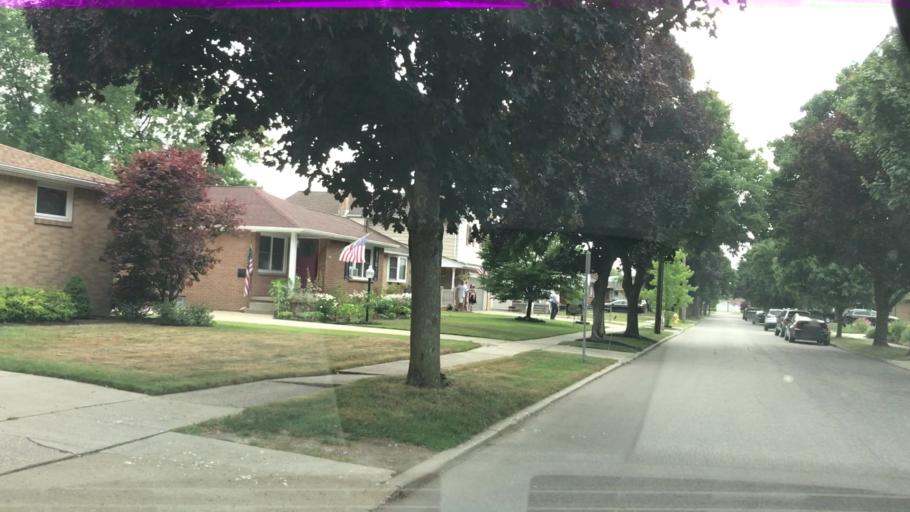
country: US
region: New York
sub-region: Erie County
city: Lancaster
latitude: 42.8913
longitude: -78.6780
